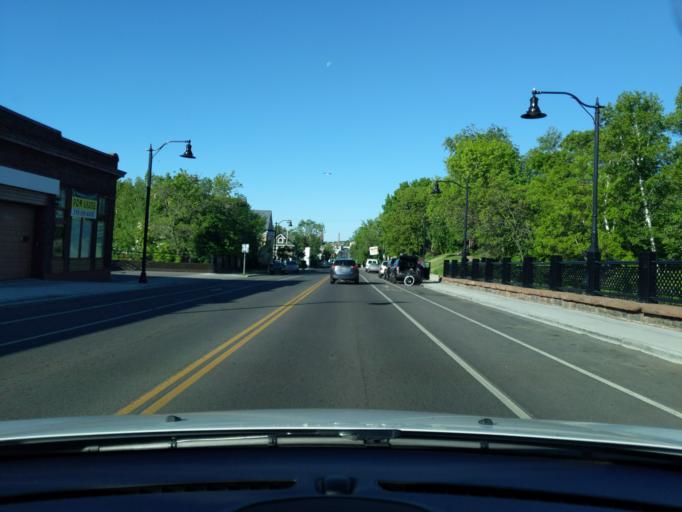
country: US
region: Minnesota
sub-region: Saint Louis County
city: Duluth
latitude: 46.8029
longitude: -92.0853
